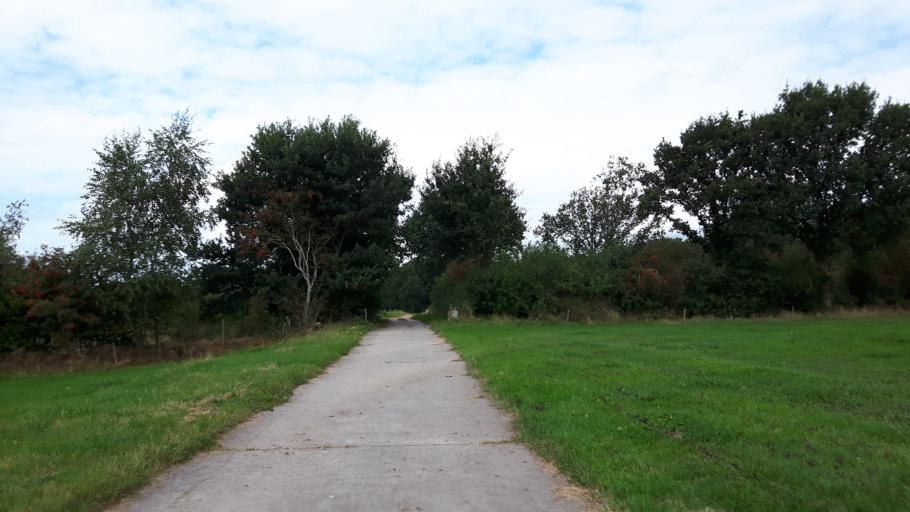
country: NL
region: Groningen
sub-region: Gemeente Leek
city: Leek
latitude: 53.0828
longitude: 6.3236
